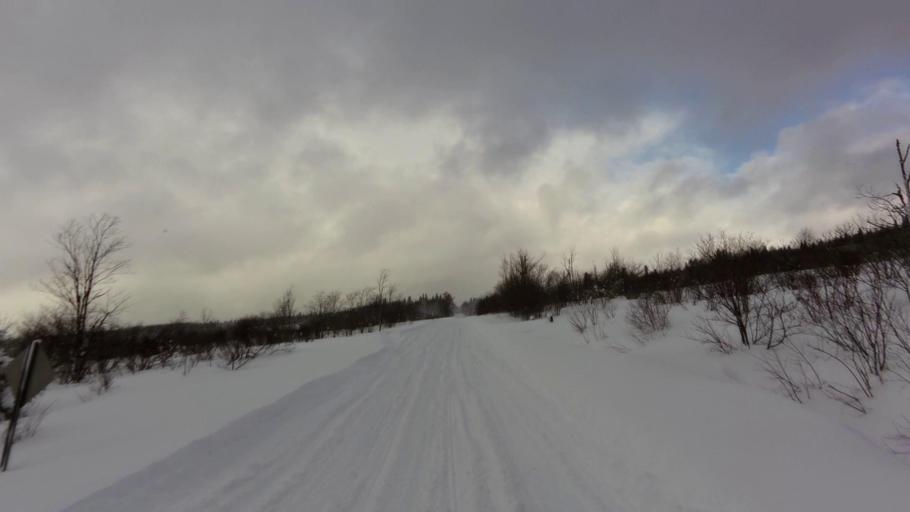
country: US
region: New York
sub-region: Lewis County
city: Lowville
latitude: 43.7341
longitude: -75.6707
